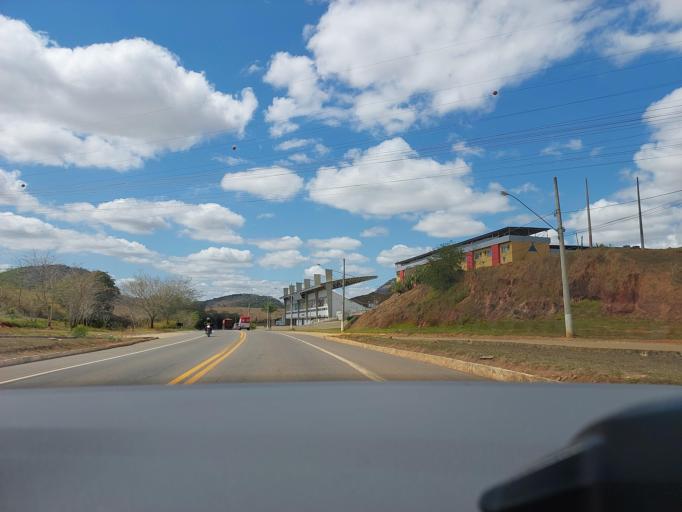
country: BR
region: Minas Gerais
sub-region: Muriae
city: Muriae
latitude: -21.1263
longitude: -42.3405
